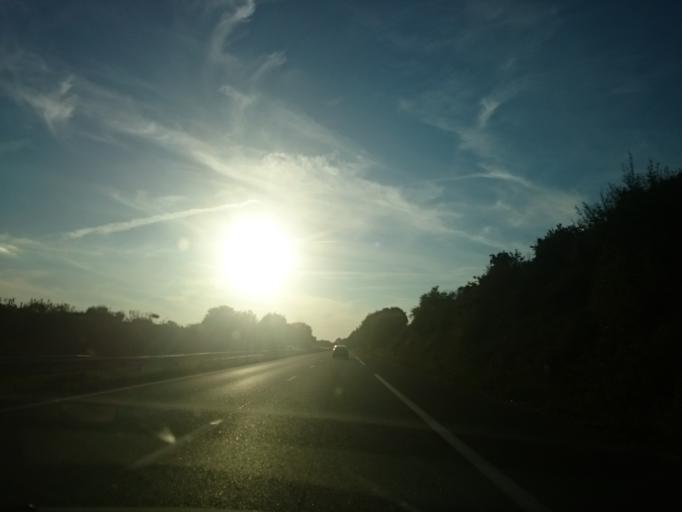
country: FR
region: Brittany
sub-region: Departement du Morbihan
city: Arradon
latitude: 47.6609
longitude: -2.8216
